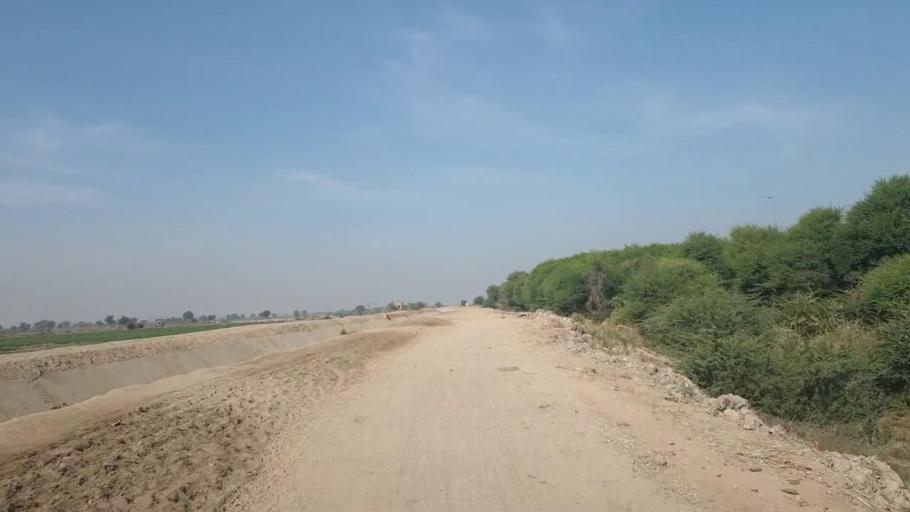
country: PK
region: Sindh
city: Matiari
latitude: 25.6839
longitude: 68.3355
